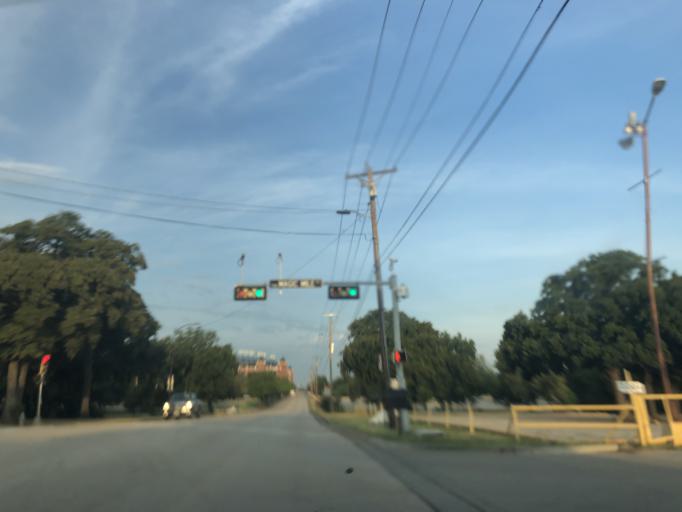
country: US
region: Texas
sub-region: Tarrant County
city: Arlington
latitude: 32.7525
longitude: -97.0747
